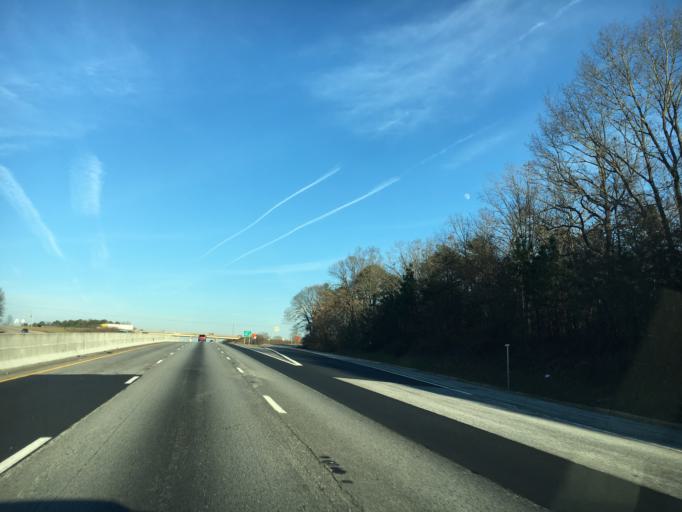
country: US
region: South Carolina
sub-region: Anderson County
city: Piedmont
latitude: 34.6727
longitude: -82.5409
